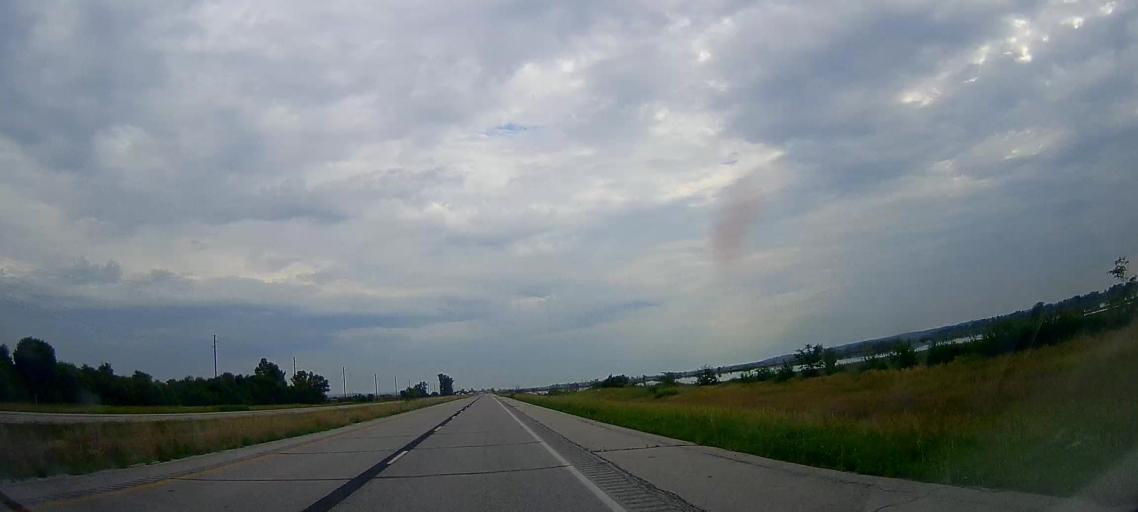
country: US
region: Iowa
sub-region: Harrison County
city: Missouri Valley
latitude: 41.4647
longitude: -95.8998
